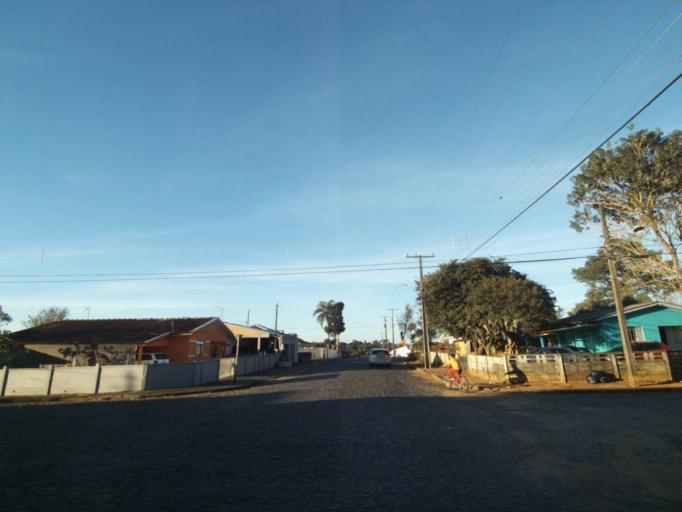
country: BR
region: Parana
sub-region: Tibagi
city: Tibagi
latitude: -24.5098
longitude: -50.4143
